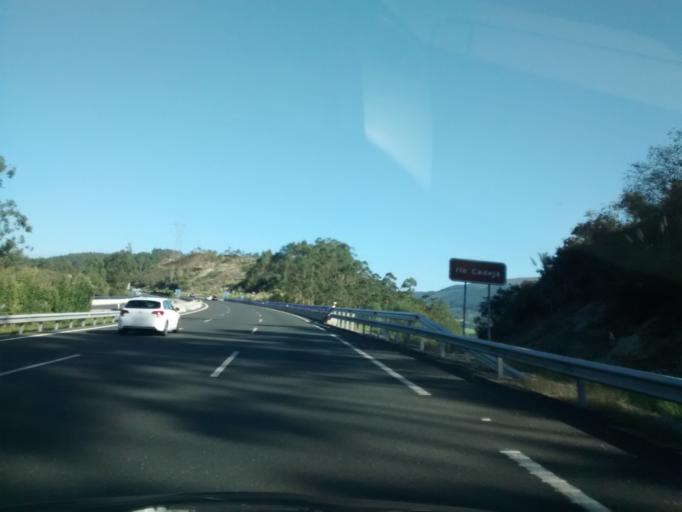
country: ES
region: Cantabria
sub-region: Provincia de Cantabria
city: Luzmela
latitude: 43.3233
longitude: -4.1829
